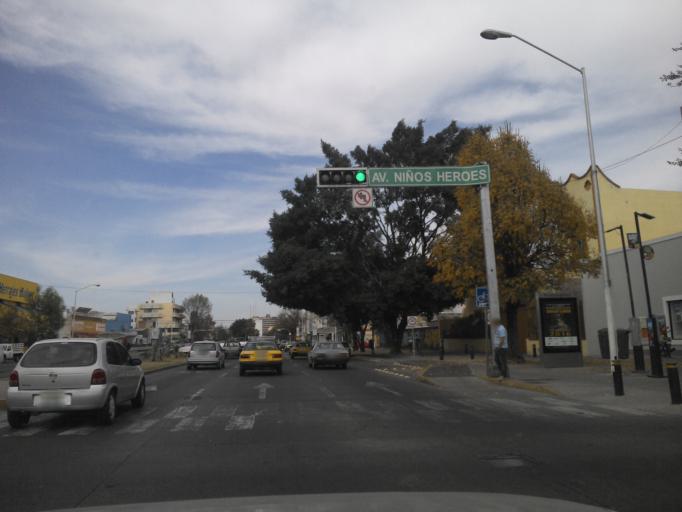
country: MX
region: Jalisco
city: Guadalajara
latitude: 20.6657
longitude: -103.3557
